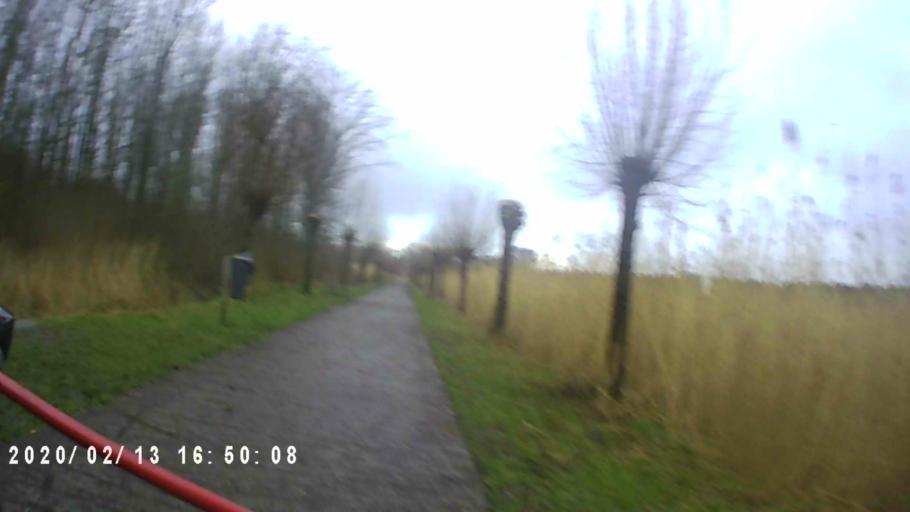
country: NL
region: Groningen
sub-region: Gemeente Groningen
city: Groningen
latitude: 53.2189
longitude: 6.5219
